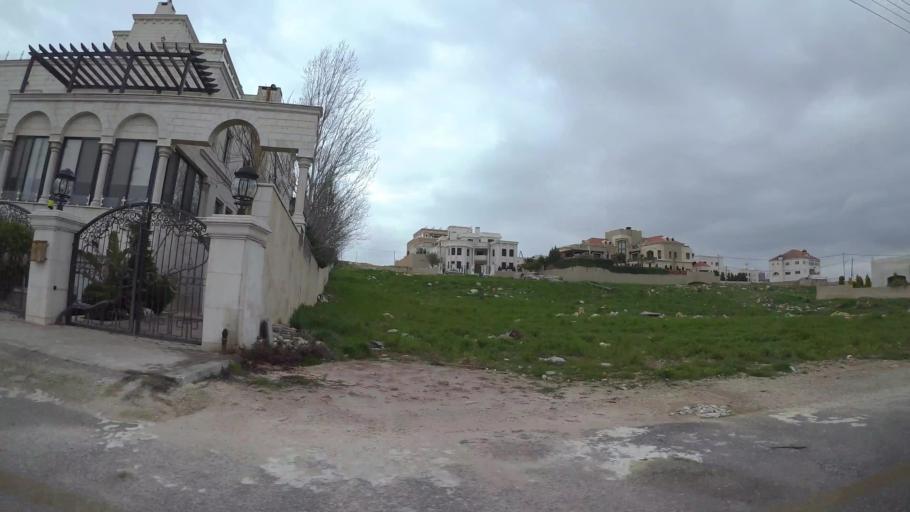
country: JO
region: Amman
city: Umm as Summaq
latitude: 31.9238
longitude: 35.8563
